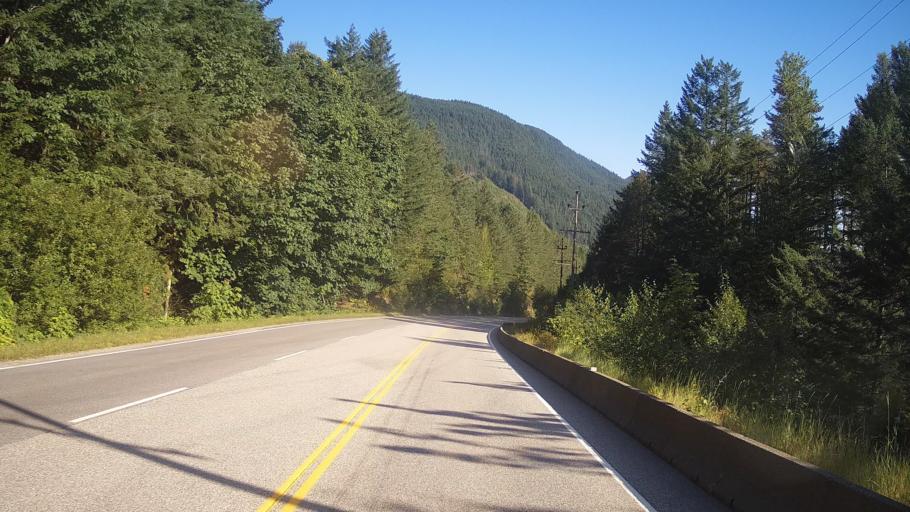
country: CA
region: British Columbia
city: Hope
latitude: 49.4215
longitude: -121.4374
